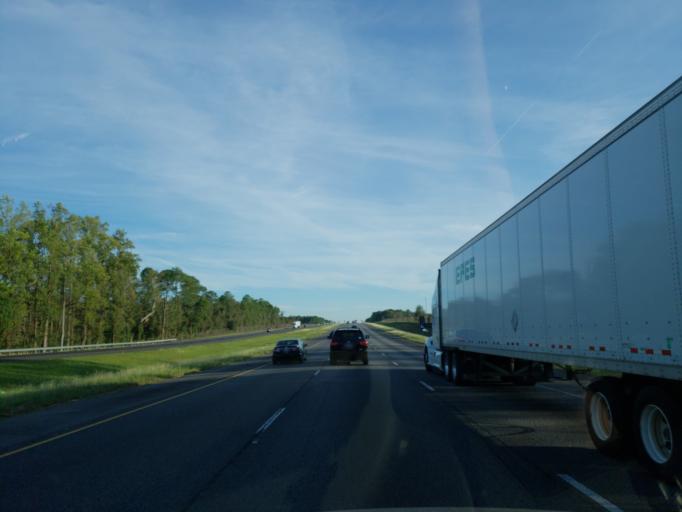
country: US
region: Georgia
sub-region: Crisp County
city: Cordele
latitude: 31.9364
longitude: -83.7460
